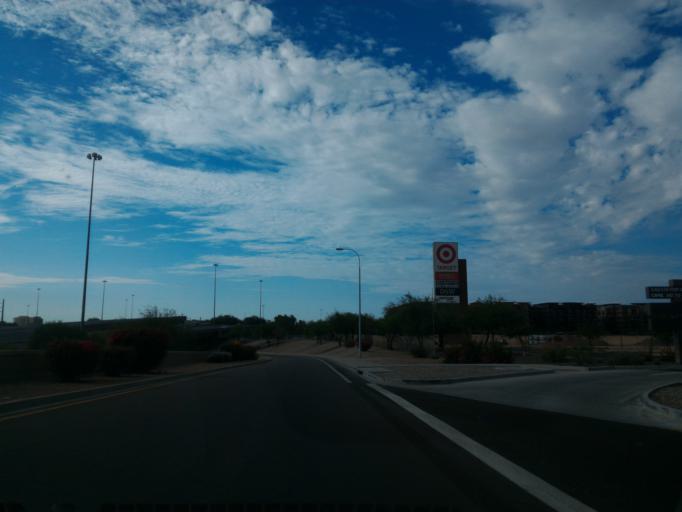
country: US
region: Arizona
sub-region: Maricopa County
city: Chandler
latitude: 33.2977
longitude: -111.8951
